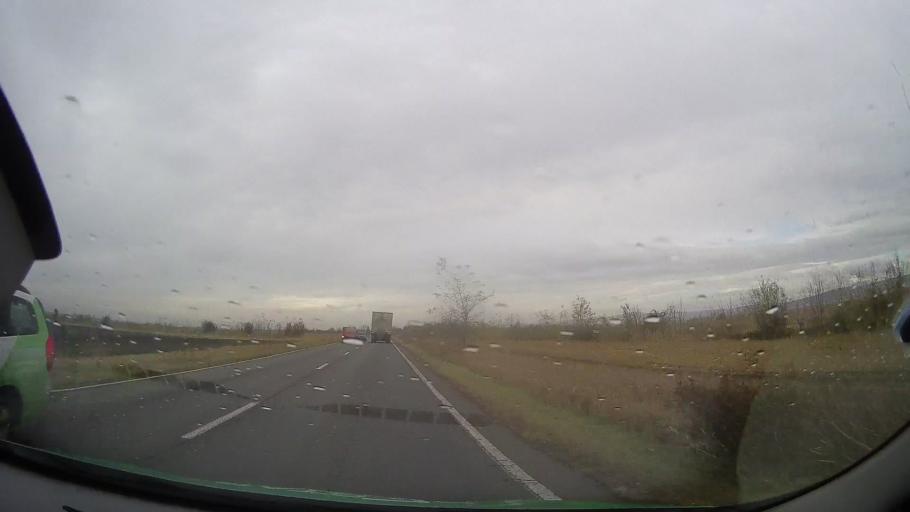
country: RO
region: Prahova
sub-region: Comuna Tomsani
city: Loloiasca
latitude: 44.9731
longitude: 26.3132
